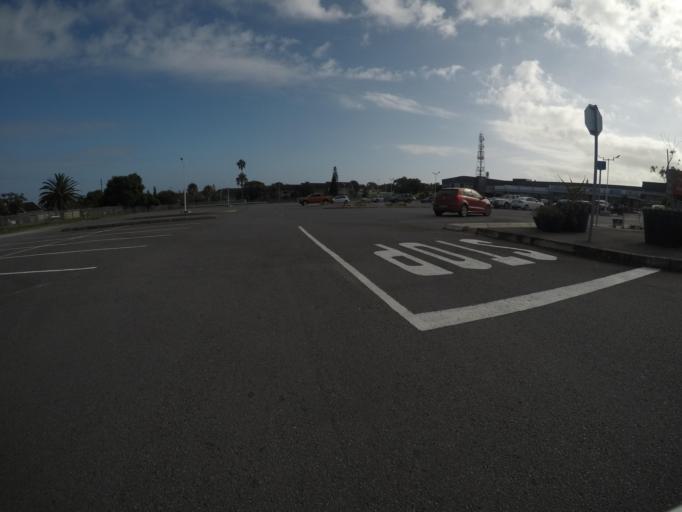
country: ZA
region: Eastern Cape
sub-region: Buffalo City Metropolitan Municipality
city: East London
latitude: -32.9678
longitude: 27.9410
